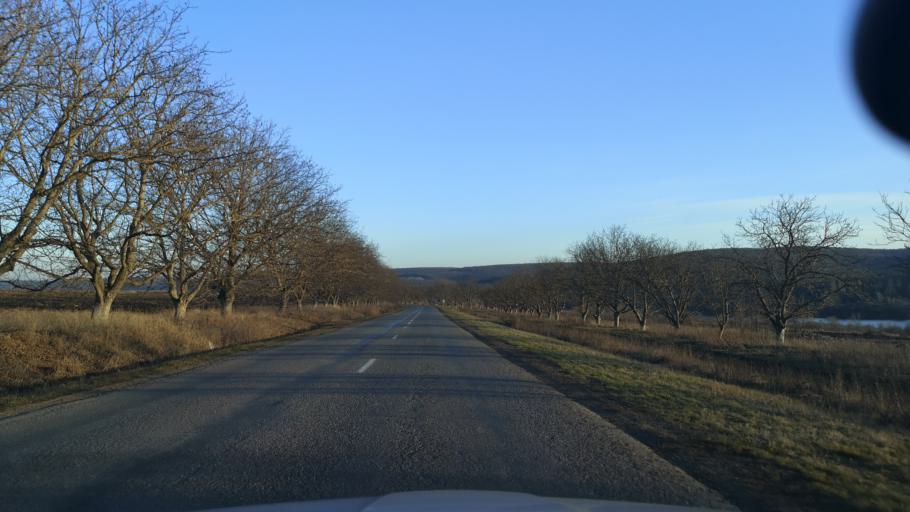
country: MD
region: Orhei
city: Orhei
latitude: 47.2865
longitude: 28.8238
